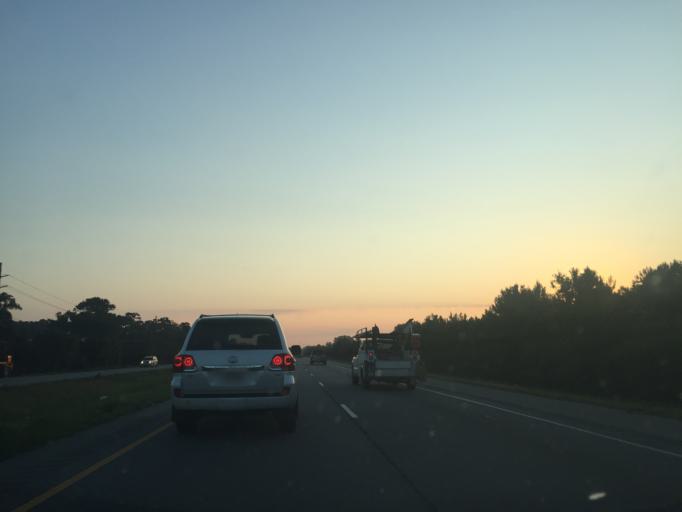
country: US
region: Georgia
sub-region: Chatham County
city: Isle of Hope
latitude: 31.9779
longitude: -81.0941
